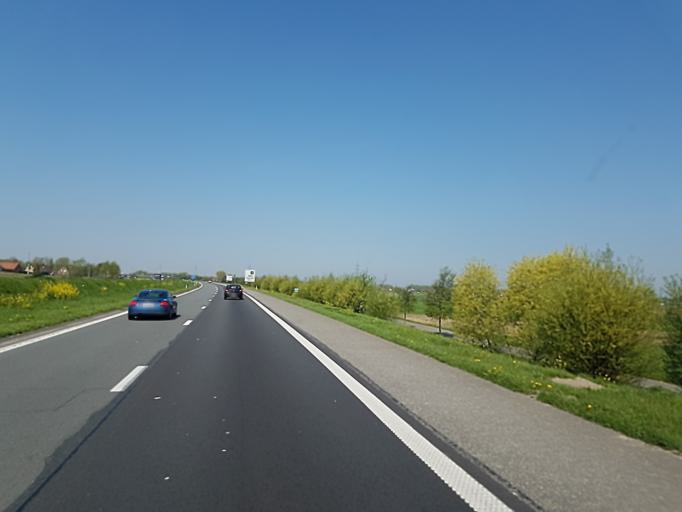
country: BE
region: Flanders
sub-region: Provincie West-Vlaanderen
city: Zonnebeke
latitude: 50.8573
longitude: 2.9702
